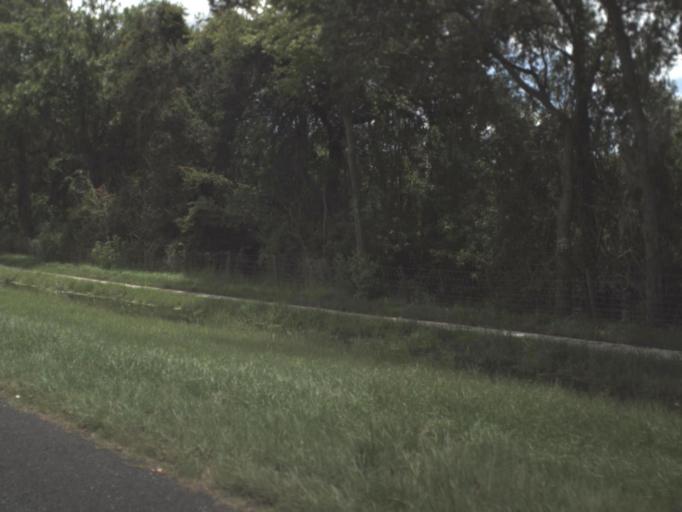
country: US
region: Florida
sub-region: Hillsborough County
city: Cheval
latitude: 28.1241
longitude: -82.5026
